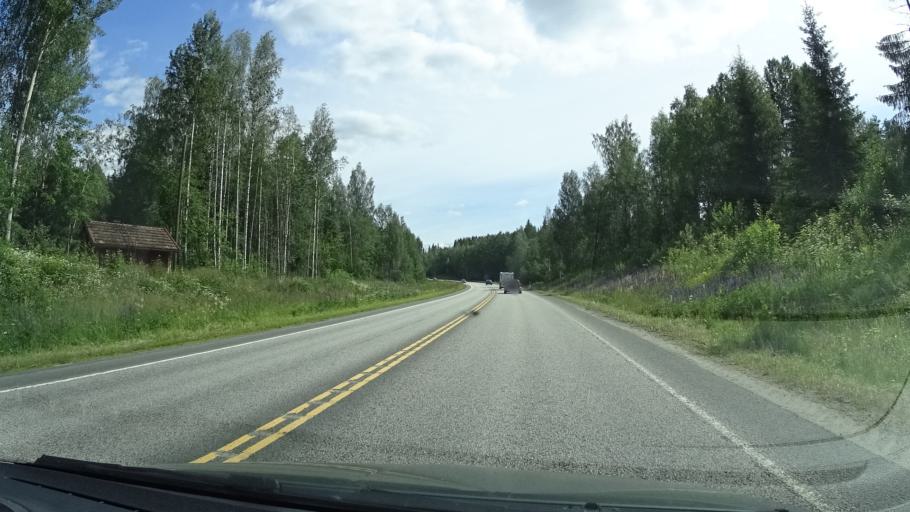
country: FI
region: Central Finland
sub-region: Jyvaeskylae
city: Jyvaeskylae
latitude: 62.2659
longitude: 25.5618
